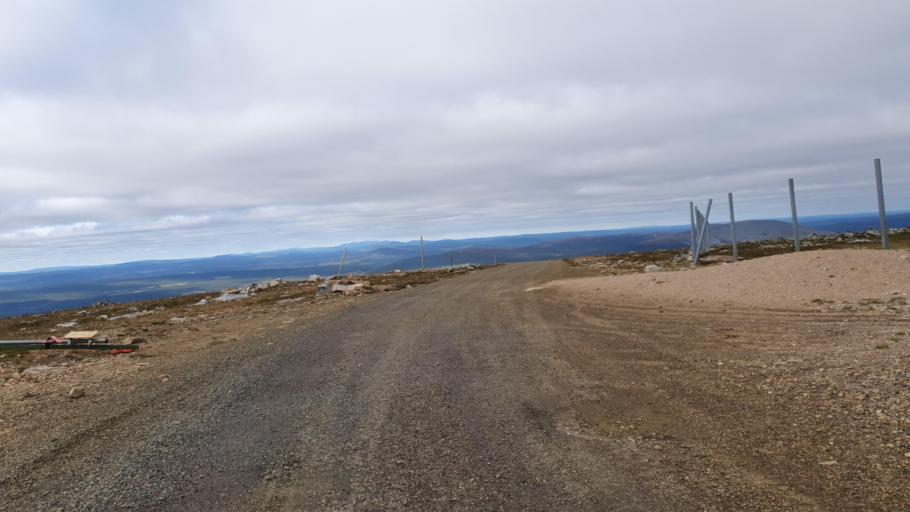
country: FI
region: Lapland
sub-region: Tunturi-Lappi
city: Kolari
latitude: 67.5669
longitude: 24.2092
